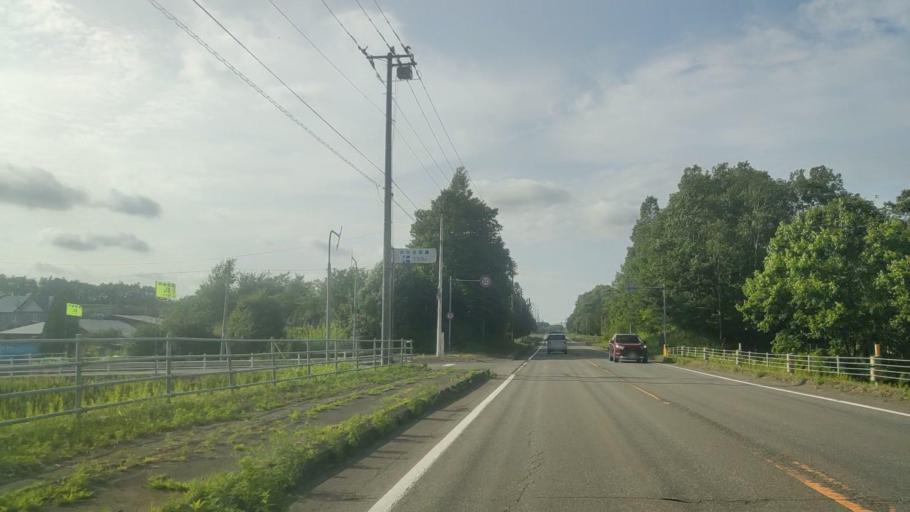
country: JP
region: Hokkaido
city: Chitose
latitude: 42.8799
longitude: 141.8154
